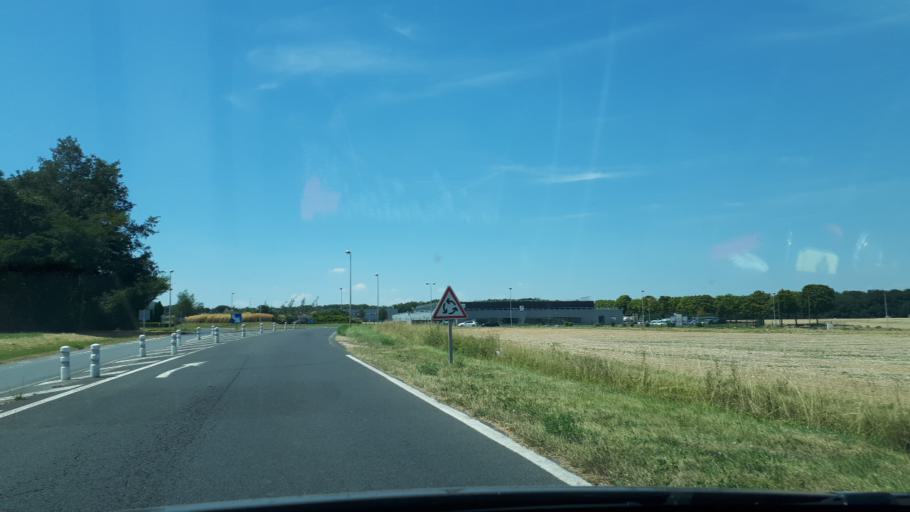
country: FR
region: Centre
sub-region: Departement du Loir-et-Cher
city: Naveil
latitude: 47.8104
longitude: 1.0309
